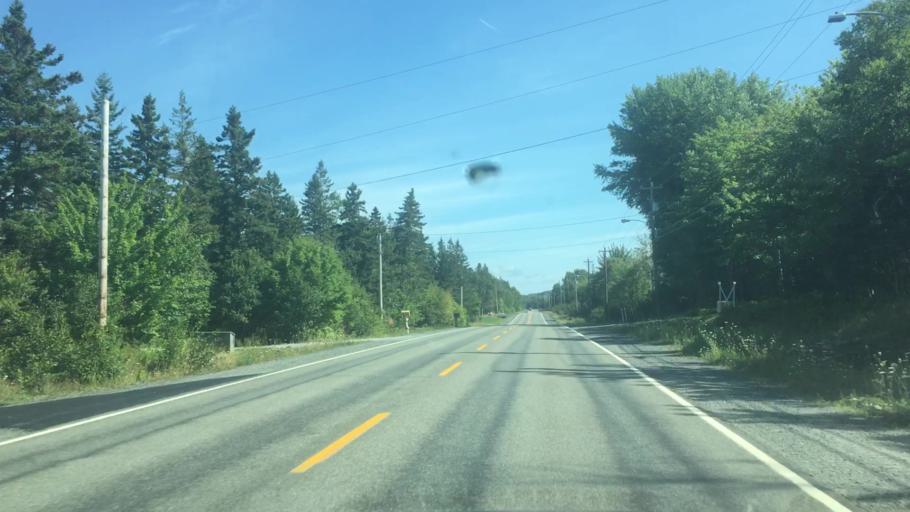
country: CA
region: Nova Scotia
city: Sydney
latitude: 45.9838
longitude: -60.4223
